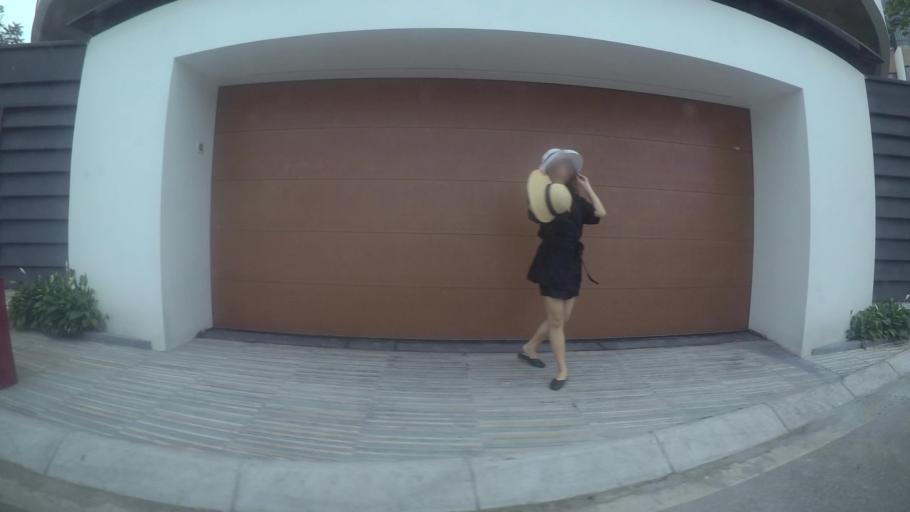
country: VN
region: Ha Noi
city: Tay Ho
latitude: 21.0546
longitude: 105.8209
